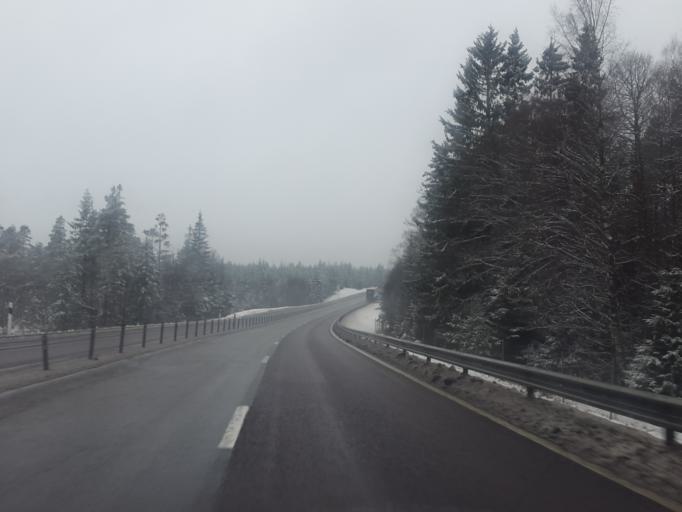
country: SE
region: Joenkoeping
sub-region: Jonkopings Kommun
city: Taberg
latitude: 57.7513
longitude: 13.9755
